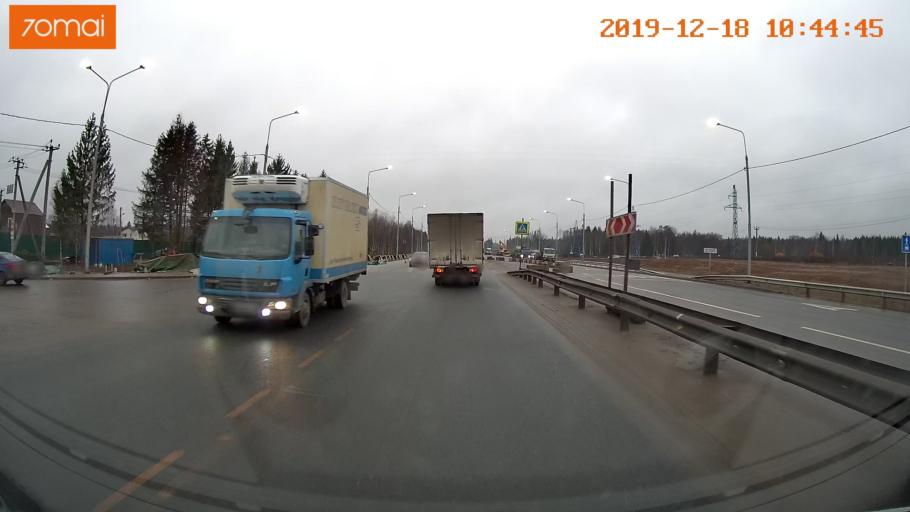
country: RU
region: Moskovskaya
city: Aprelevka
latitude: 55.4744
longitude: 37.0689
